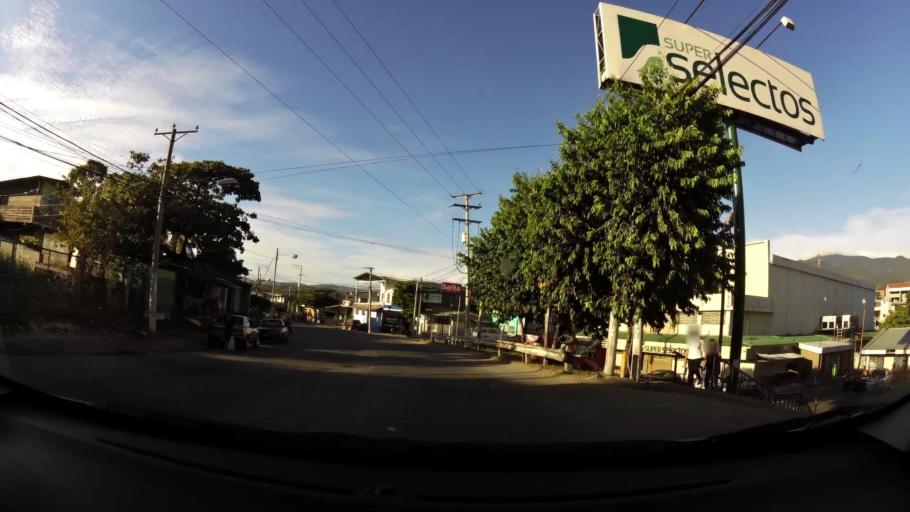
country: SV
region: Santa Ana
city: Metapan
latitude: 14.3317
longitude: -89.4422
